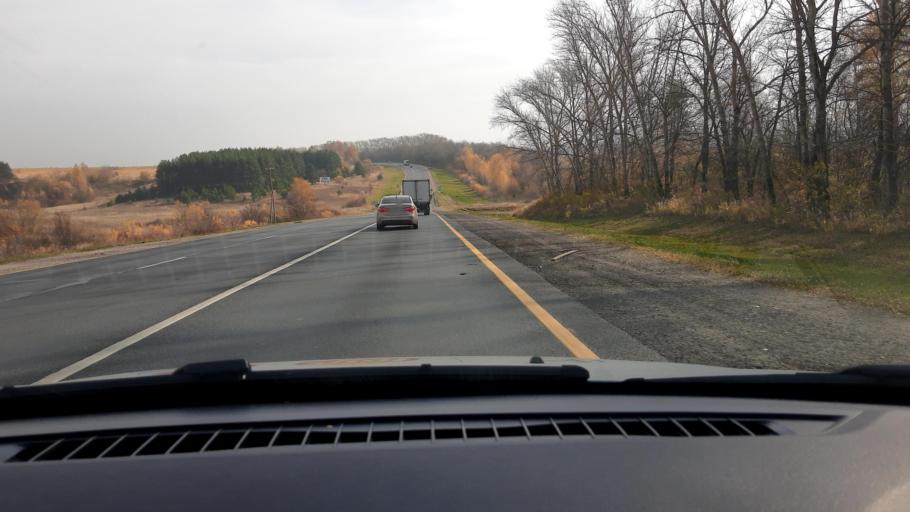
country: RU
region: Nizjnij Novgorod
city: Pamyat' Parizhskoy Kommuny
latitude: 56.0493
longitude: 44.4158
